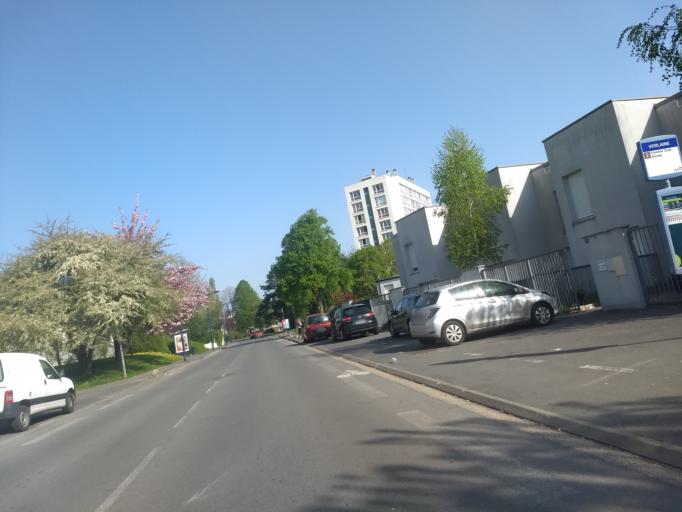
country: FR
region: Nord-Pas-de-Calais
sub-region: Departement du Pas-de-Calais
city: Anzin-Saint-Aubin
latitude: 50.3025
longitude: 2.7464
